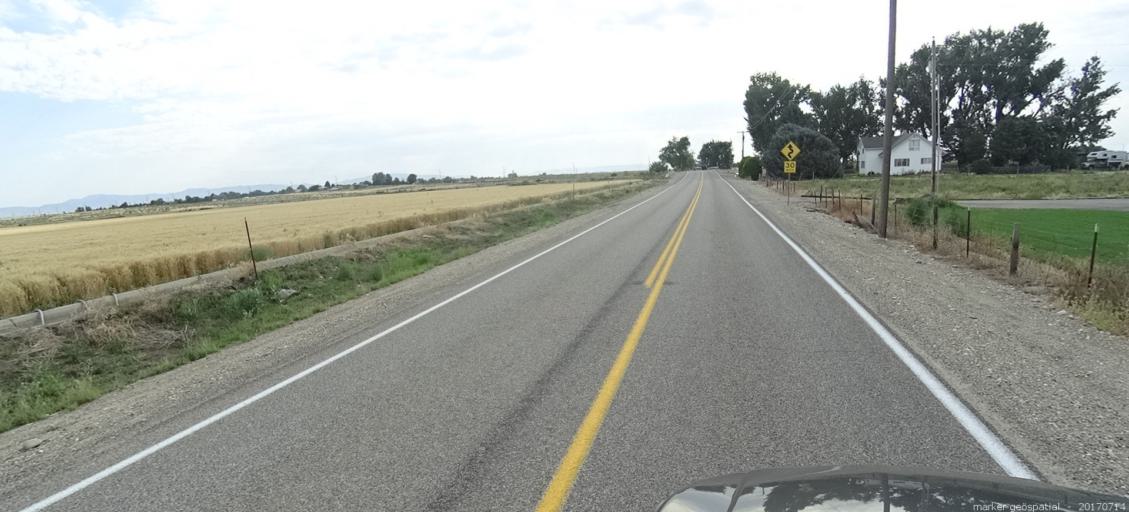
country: US
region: Idaho
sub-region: Ada County
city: Kuna
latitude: 43.4736
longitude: -116.3427
